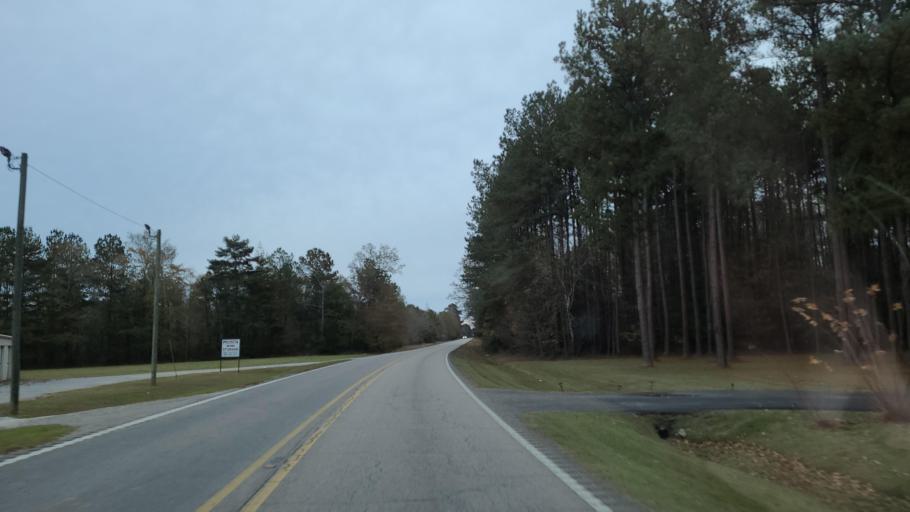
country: US
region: Mississippi
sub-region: Clarke County
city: Stonewall
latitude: 32.0388
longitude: -88.8800
